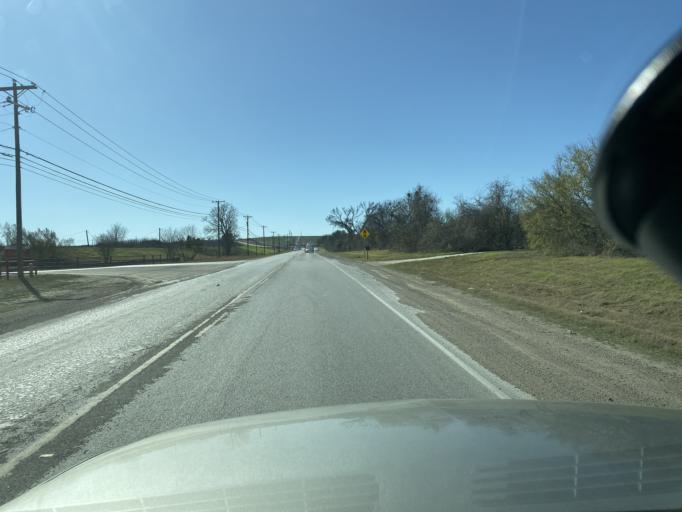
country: US
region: Texas
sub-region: Travis County
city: Garfield
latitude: 30.1705
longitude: -97.6551
